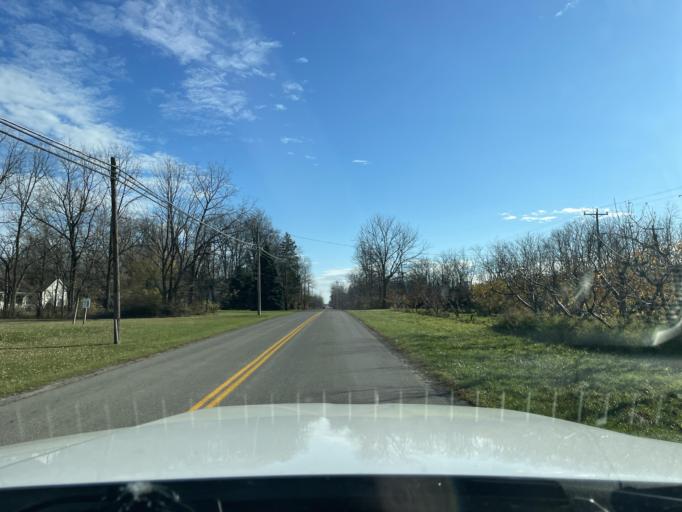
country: US
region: New York
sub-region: Niagara County
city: Middleport
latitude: 43.2063
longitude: -78.5242
